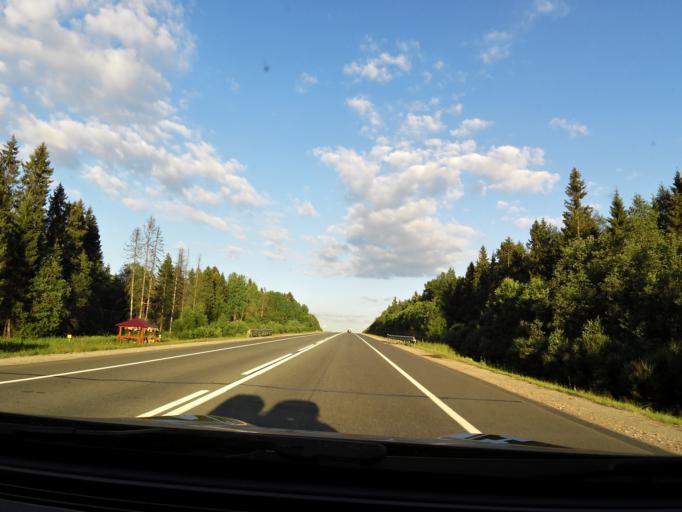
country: RU
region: Vologda
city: Vologda
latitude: 59.0654
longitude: 40.0452
